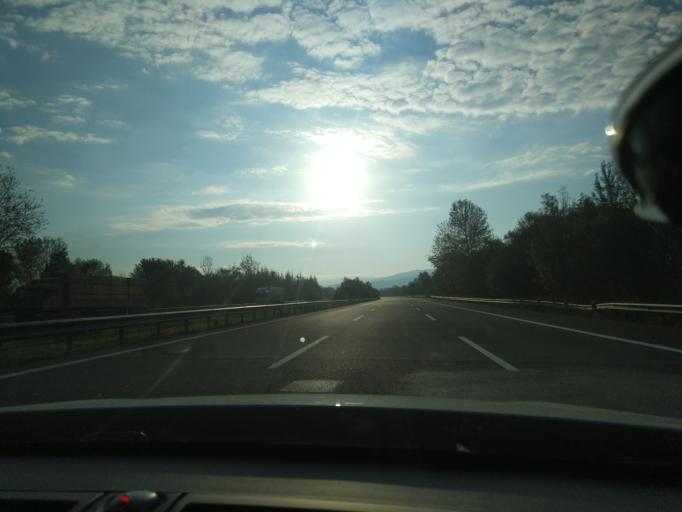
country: TR
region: Duzce
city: Duzce
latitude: 40.7956
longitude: 31.1955
